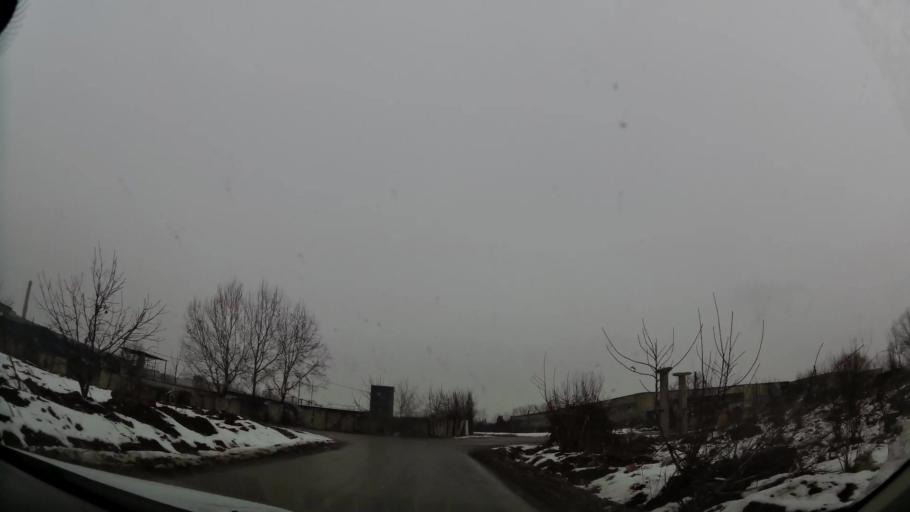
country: RO
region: Ilfov
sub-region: Comuna Pantelimon
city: Pantelimon
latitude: 44.4198
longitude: 26.1919
